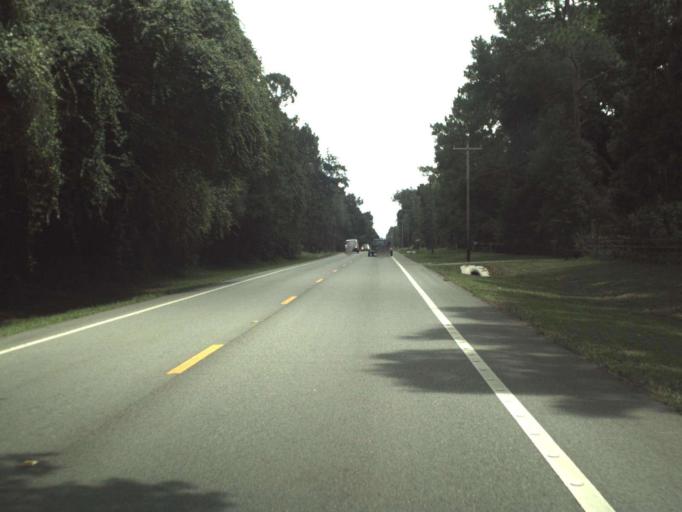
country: US
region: Florida
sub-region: Sumter County
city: Bushnell
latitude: 28.6852
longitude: -82.1042
